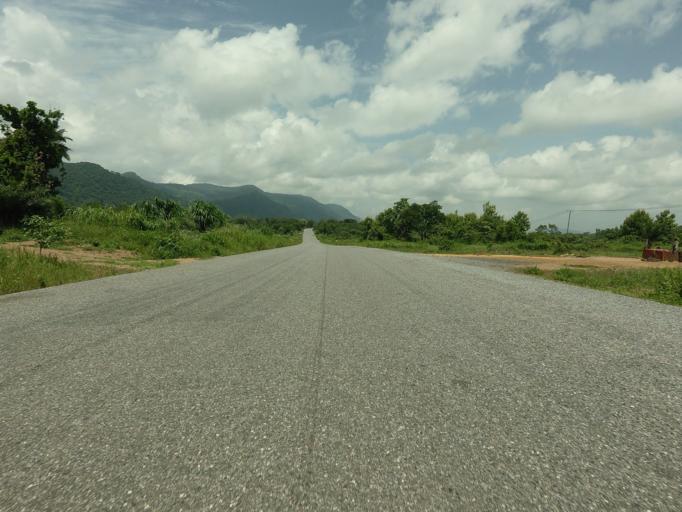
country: GH
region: Volta
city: Kpandu
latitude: 6.8548
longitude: 0.3939
